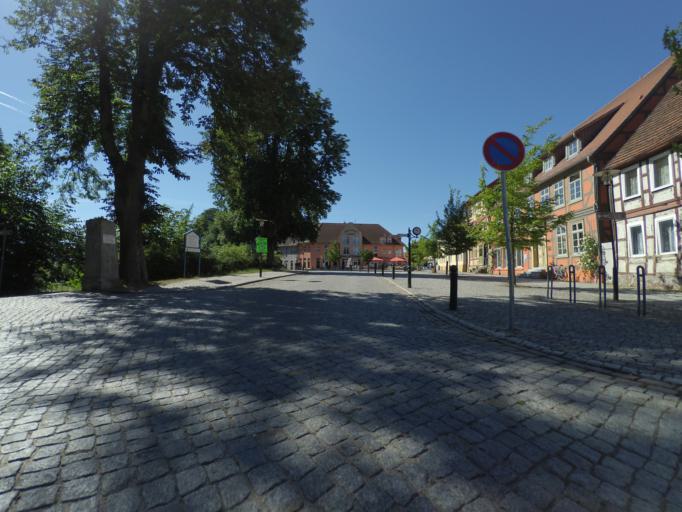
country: DE
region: Mecklenburg-Vorpommern
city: Plau am See
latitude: 53.4595
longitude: 12.2647
